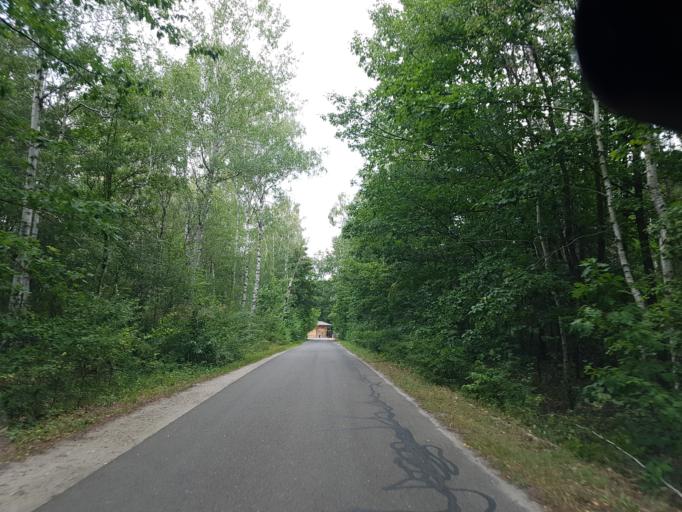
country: DE
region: Brandenburg
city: Sallgast
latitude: 51.5686
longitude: 13.8642
